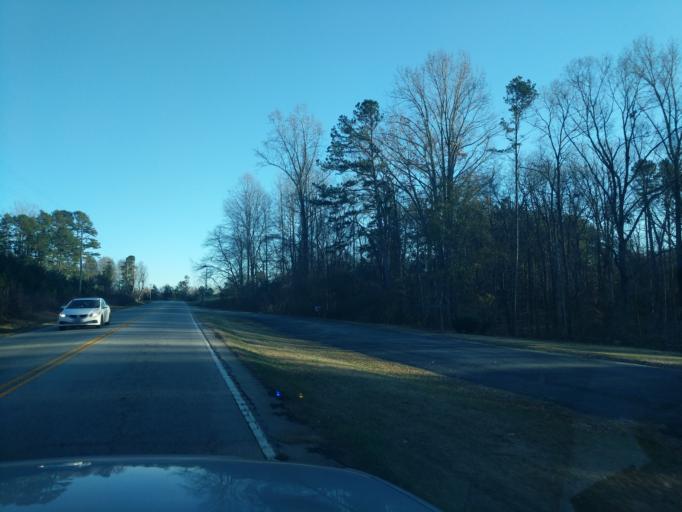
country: US
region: South Carolina
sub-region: Oconee County
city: Westminster
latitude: 34.6422
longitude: -83.0645
